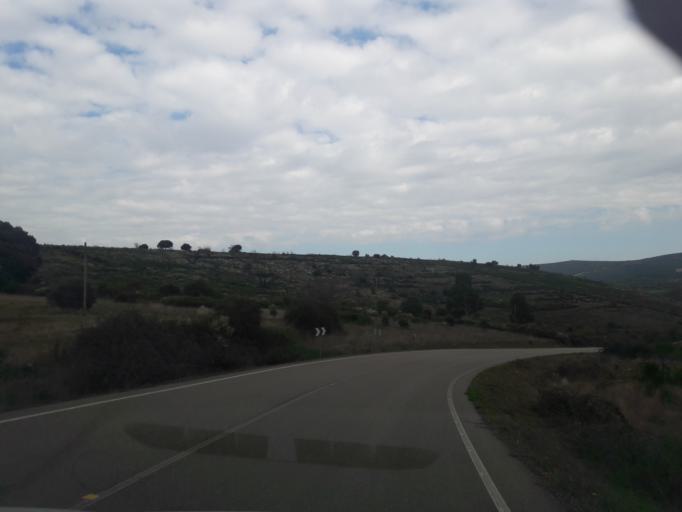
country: ES
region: Castille and Leon
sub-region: Provincia de Salamanca
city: Serradilla del Llano
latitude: 40.5076
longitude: -6.3628
